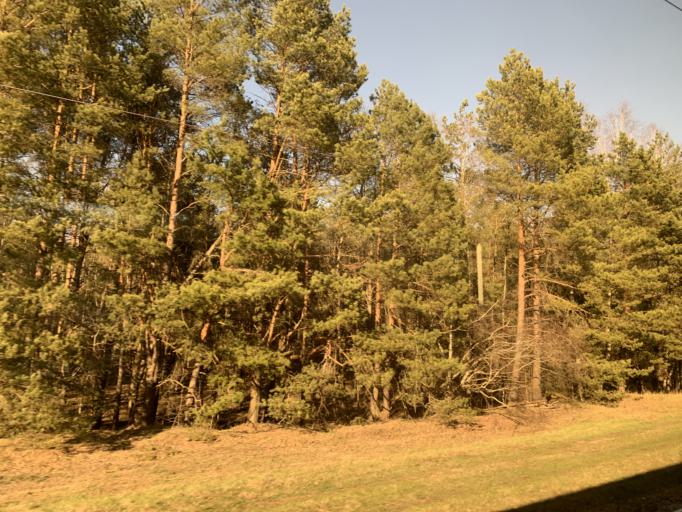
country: BY
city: Soly
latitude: 54.4928
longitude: 26.2855
